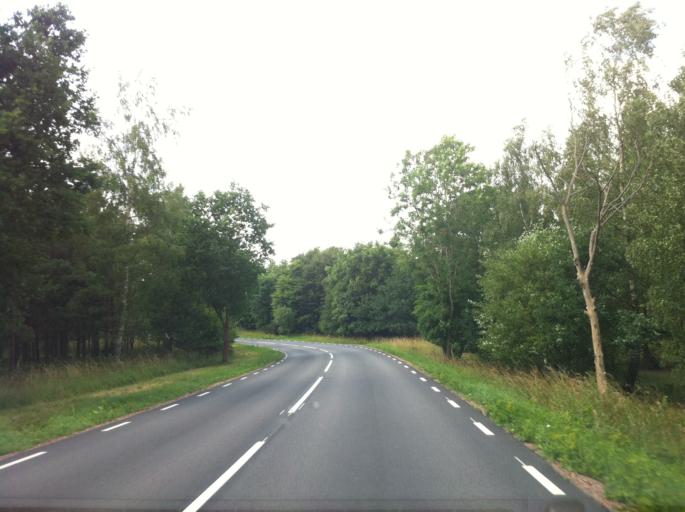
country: SE
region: Skane
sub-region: Trelleborgs Kommun
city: Anderslov
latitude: 55.4877
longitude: 13.3686
